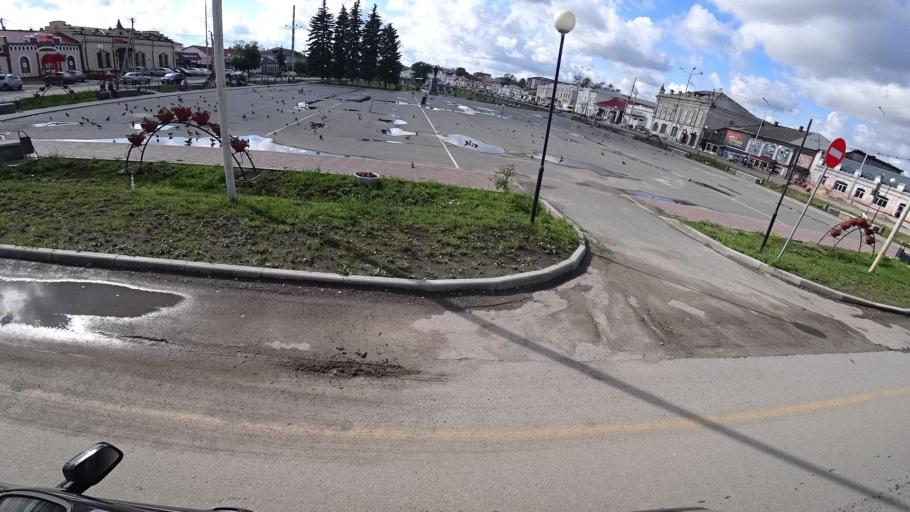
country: RU
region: Sverdlovsk
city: Kamyshlov
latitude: 56.8437
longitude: 62.7081
